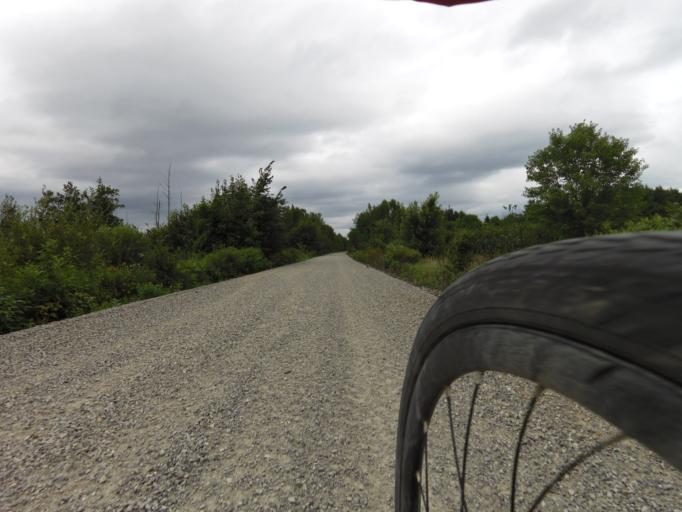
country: CA
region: Ontario
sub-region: Lanark County
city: Smiths Falls
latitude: 44.9605
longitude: -76.0503
